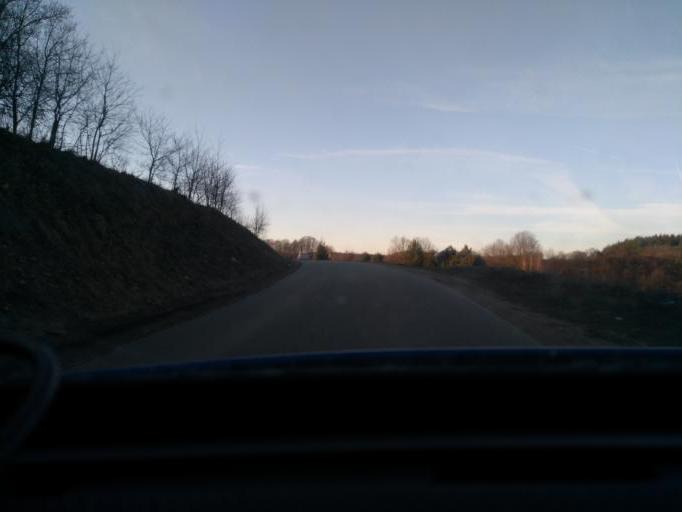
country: PL
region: Pomeranian Voivodeship
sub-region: Powiat kartuski
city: Przodkowo
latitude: 54.3687
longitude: 18.2676
